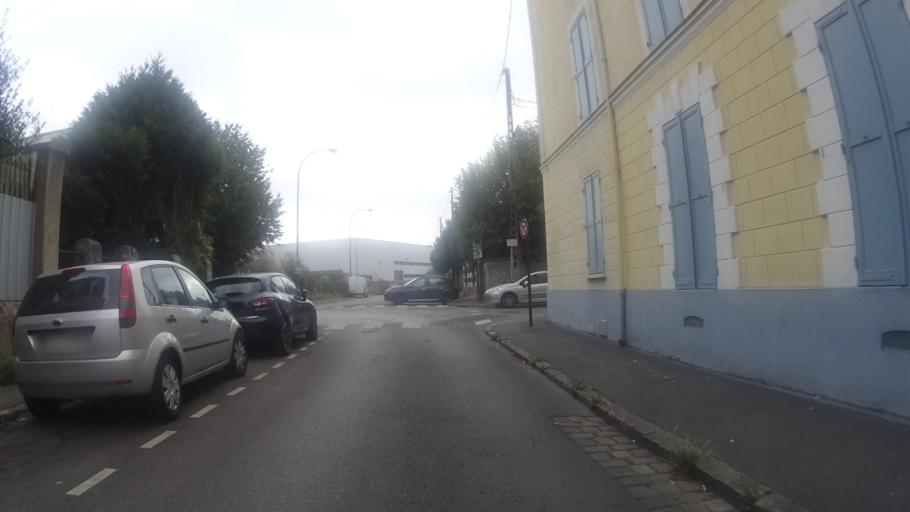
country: FR
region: Ile-de-France
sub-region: Departement de l'Essonne
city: Corbeil-Essonnes
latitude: 48.6120
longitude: 2.4760
